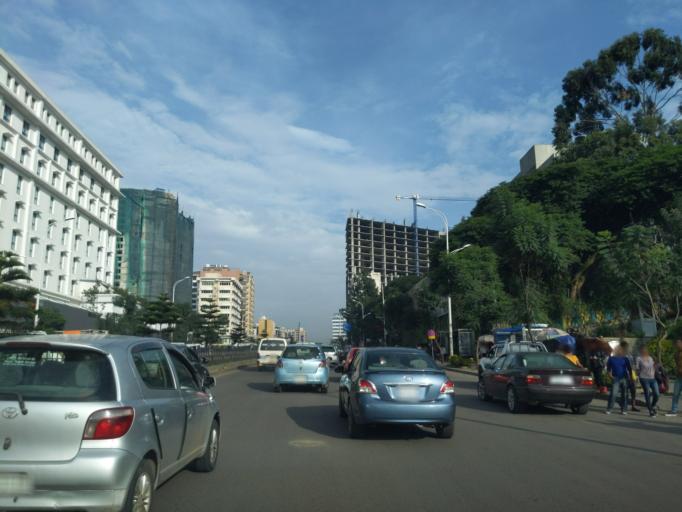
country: ET
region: Adis Abeba
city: Addis Ababa
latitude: 9.0104
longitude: 38.7632
